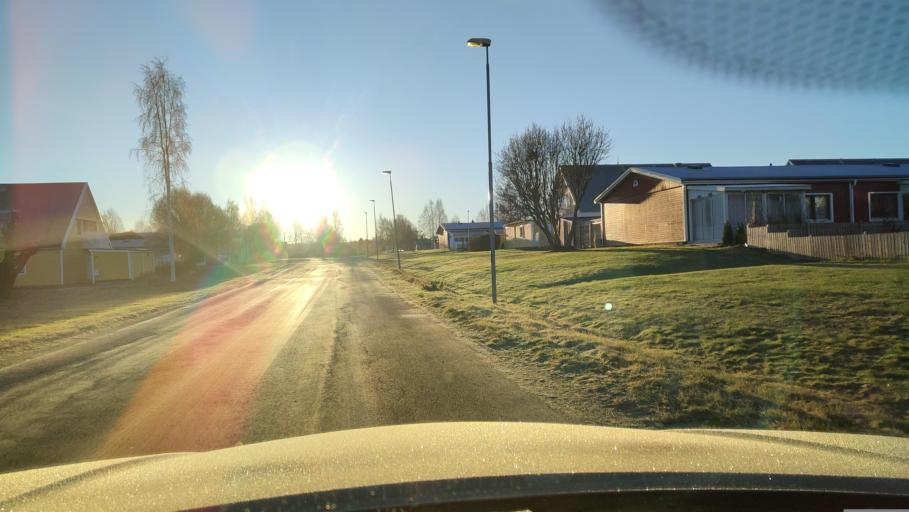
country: SE
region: Vaesterbotten
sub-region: Skelleftea Kommun
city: Skelleftea
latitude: 64.7433
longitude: 20.9833
